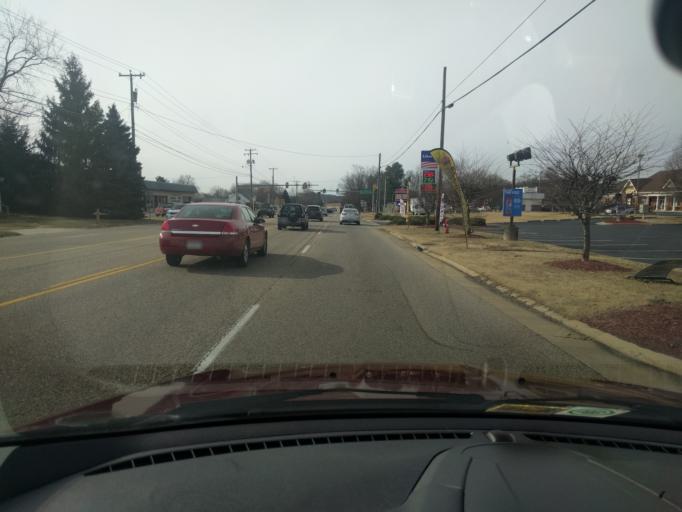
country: US
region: Virginia
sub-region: Augusta County
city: Stuarts Draft
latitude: 38.0429
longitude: -79.0086
